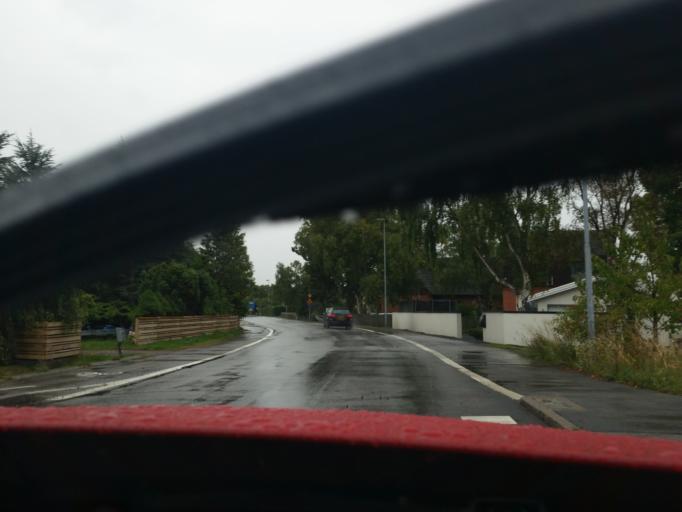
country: SE
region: Skane
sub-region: Malmo
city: Bunkeflostrand
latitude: 55.5312
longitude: 12.9239
